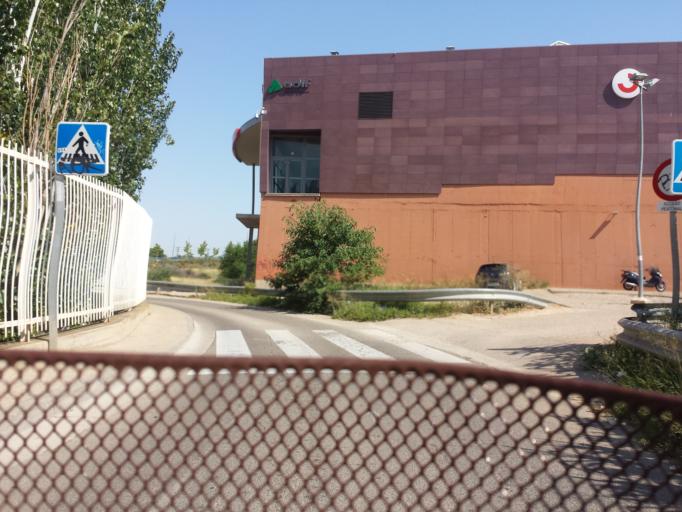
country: ES
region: Aragon
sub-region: Provincia de Zaragoza
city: Zaragoza
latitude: 41.6337
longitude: -0.8682
